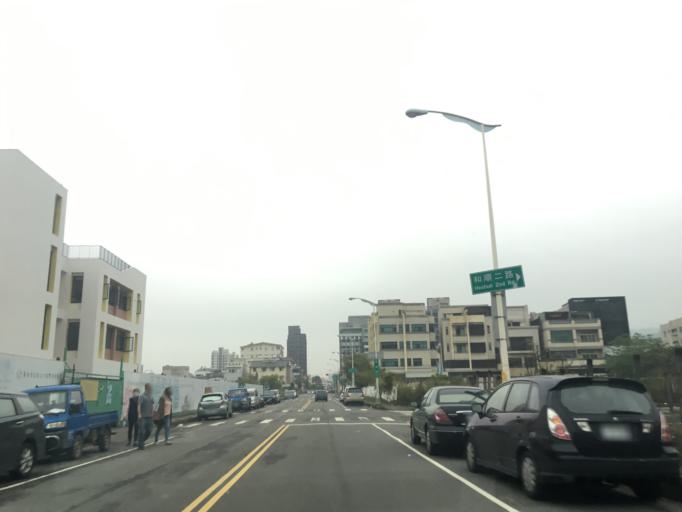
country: TW
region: Taiwan
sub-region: Taichung City
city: Taichung
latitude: 24.1680
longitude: 120.7226
